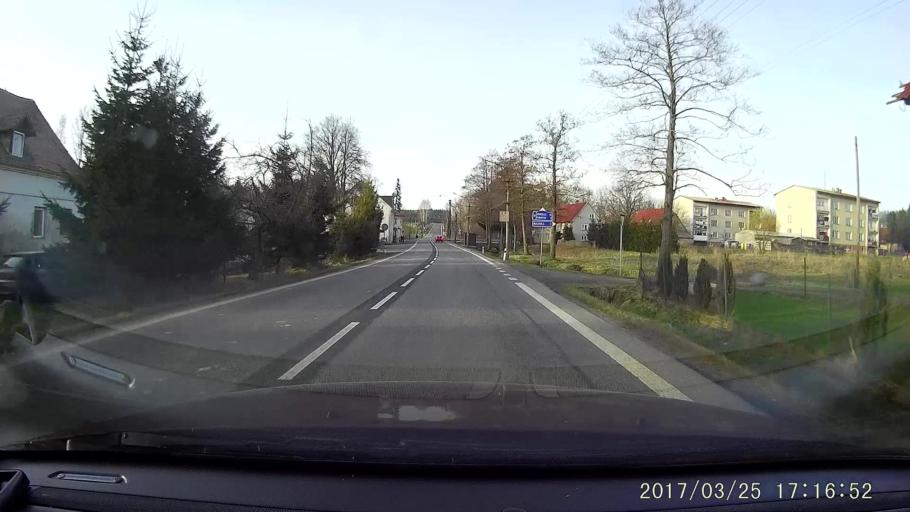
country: CZ
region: Liberecky
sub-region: Okres Liberec
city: Frydlant
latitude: 50.9616
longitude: 15.0966
